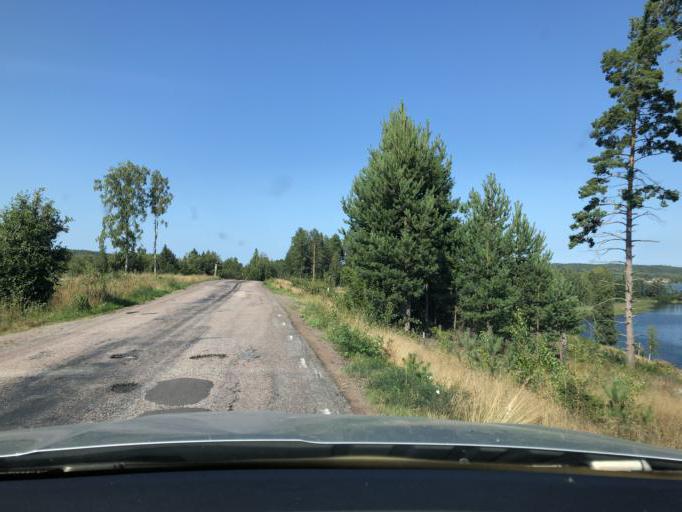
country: SE
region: Dalarna
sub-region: Hedemora Kommun
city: Hedemora
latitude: 60.3314
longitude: 15.9189
